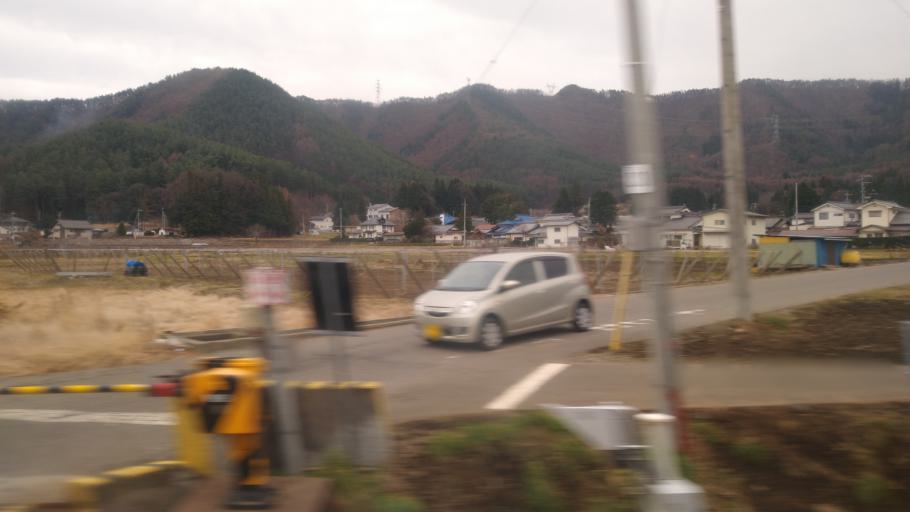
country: JP
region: Nagano
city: Shiojiri
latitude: 36.0984
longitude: 137.9299
